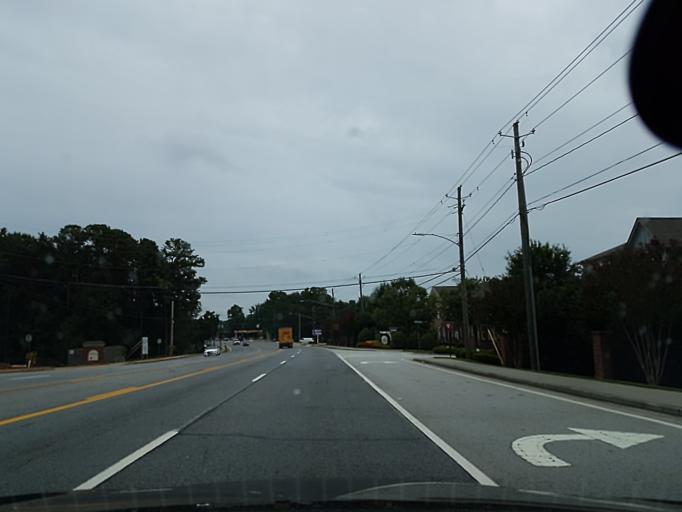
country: US
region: Georgia
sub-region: DeKalb County
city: Clarkston
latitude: 33.8186
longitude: -84.2664
